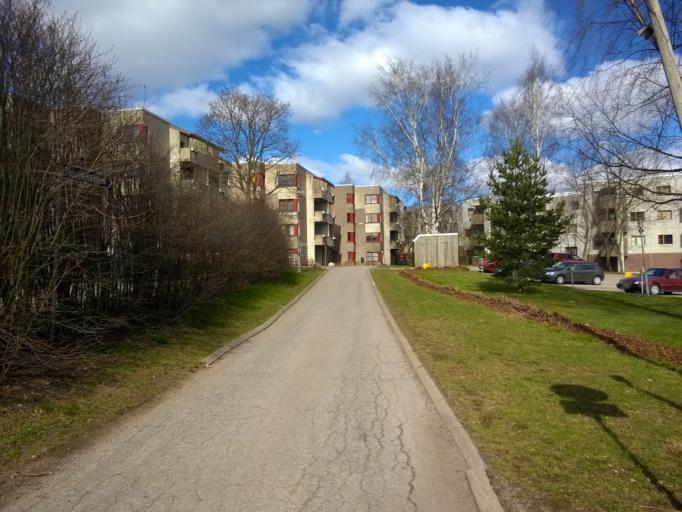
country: FI
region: Uusimaa
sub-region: Helsinki
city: Vantaa
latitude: 60.2309
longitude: 25.0176
